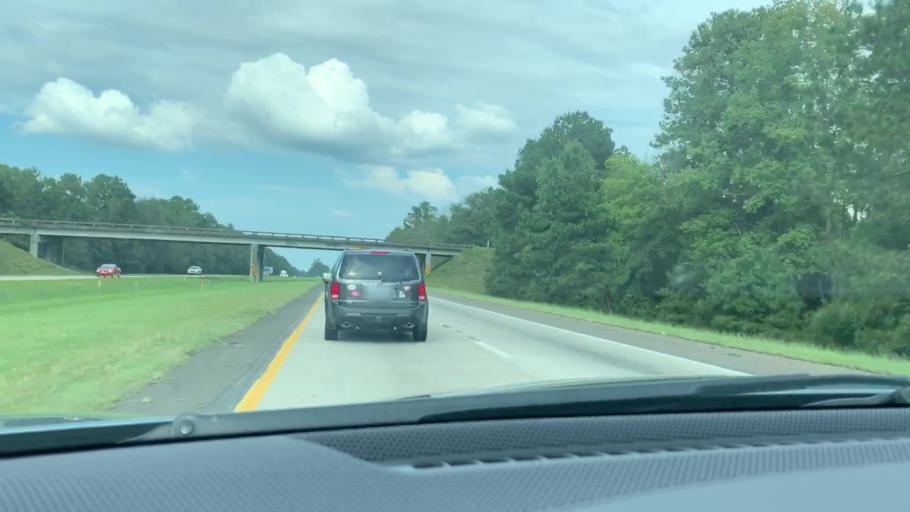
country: US
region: South Carolina
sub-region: Colleton County
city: Walterboro
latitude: 32.8385
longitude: -80.7410
